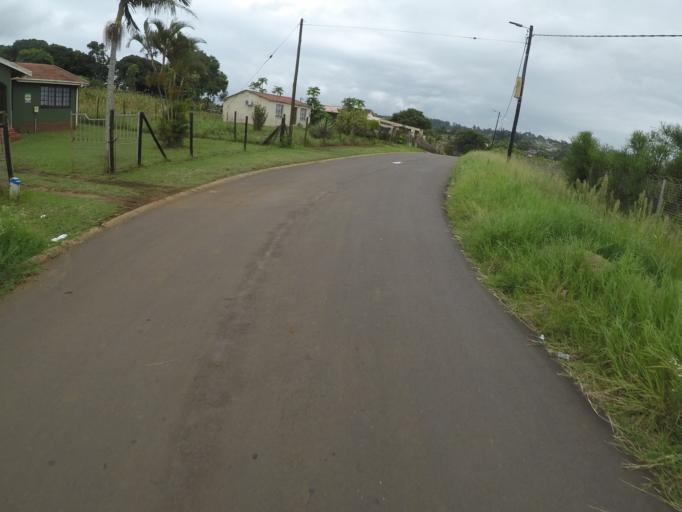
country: ZA
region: KwaZulu-Natal
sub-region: uThungulu District Municipality
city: Empangeni
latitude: -28.7683
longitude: 31.8664
